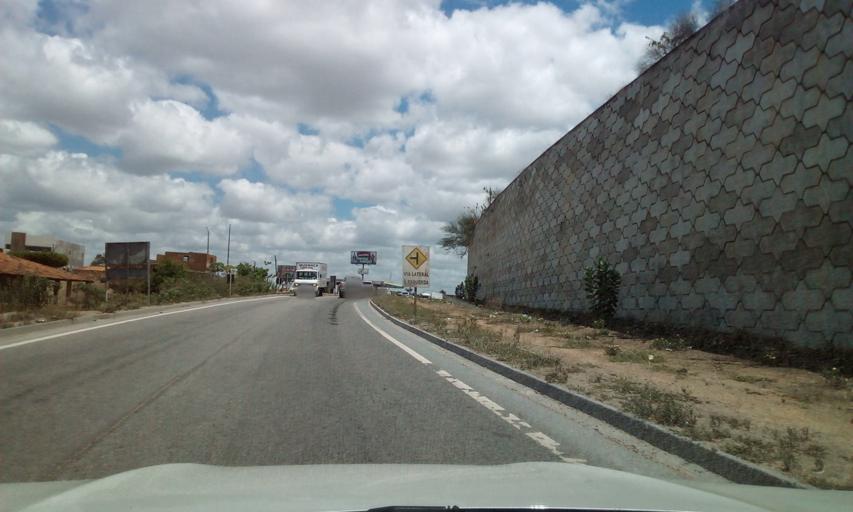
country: BR
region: Alagoas
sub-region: Porto Real Do Colegio
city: Porto Real do Colegio
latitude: -10.1830
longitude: -36.8291
